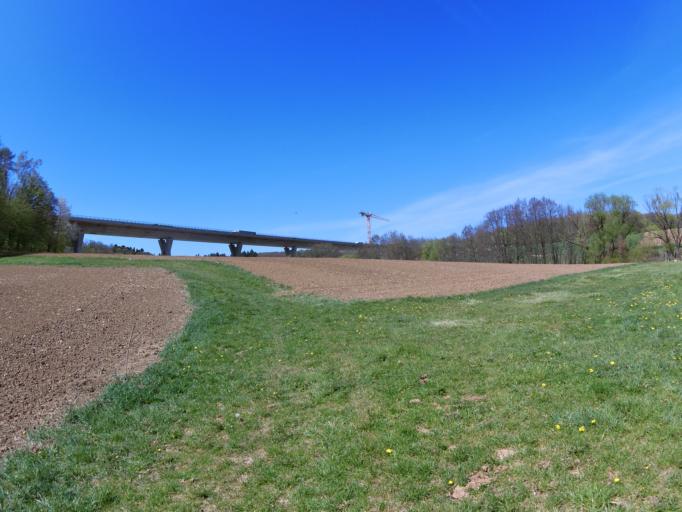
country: DE
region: Bavaria
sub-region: Regierungsbezirk Unterfranken
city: Estenfeld
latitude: 49.8576
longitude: 9.9985
